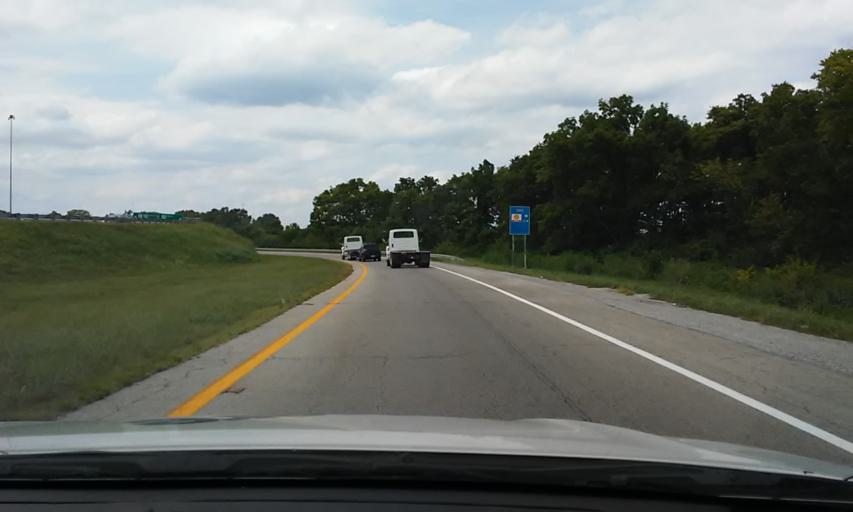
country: US
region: Ohio
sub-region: Clark County
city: Park Layne
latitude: 39.8665
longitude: -84.0521
